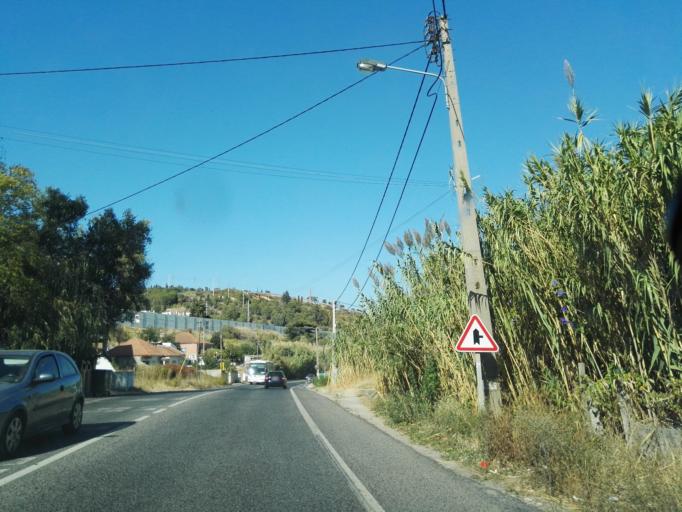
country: PT
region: Lisbon
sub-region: Vila Franca de Xira
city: Sobralinho
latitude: 38.9158
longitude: -9.0210
